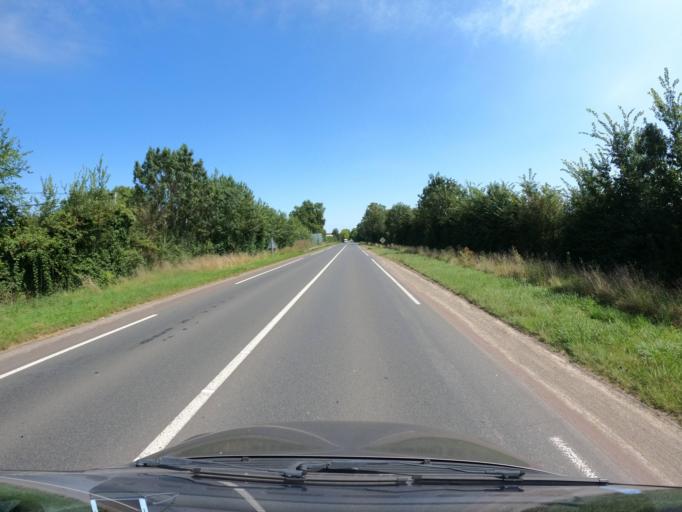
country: FR
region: Poitou-Charentes
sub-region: Departement des Deux-Sevres
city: Bessines
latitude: 46.2904
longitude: -0.5081
